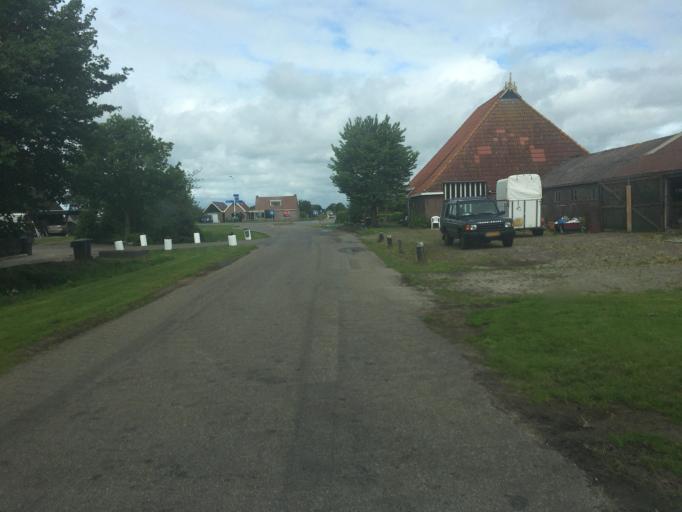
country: NL
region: Friesland
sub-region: Gemeente Skarsterlan
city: Oudehaske
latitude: 52.9184
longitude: 5.8532
